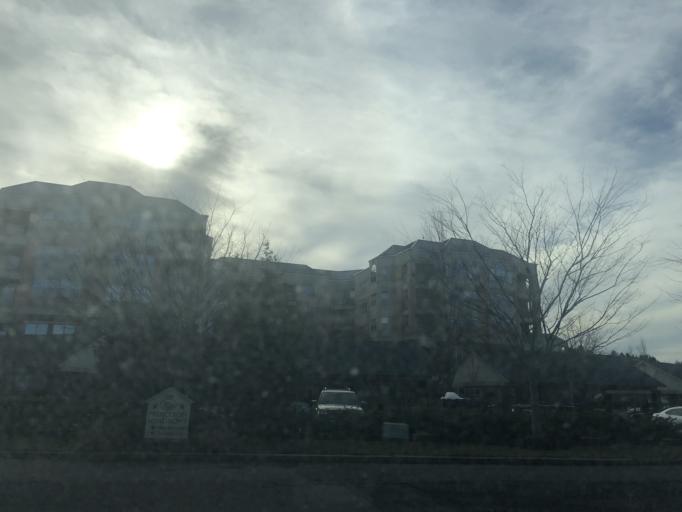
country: US
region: New Jersey
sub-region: Somerset County
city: Kingston
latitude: 40.3580
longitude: -74.6173
